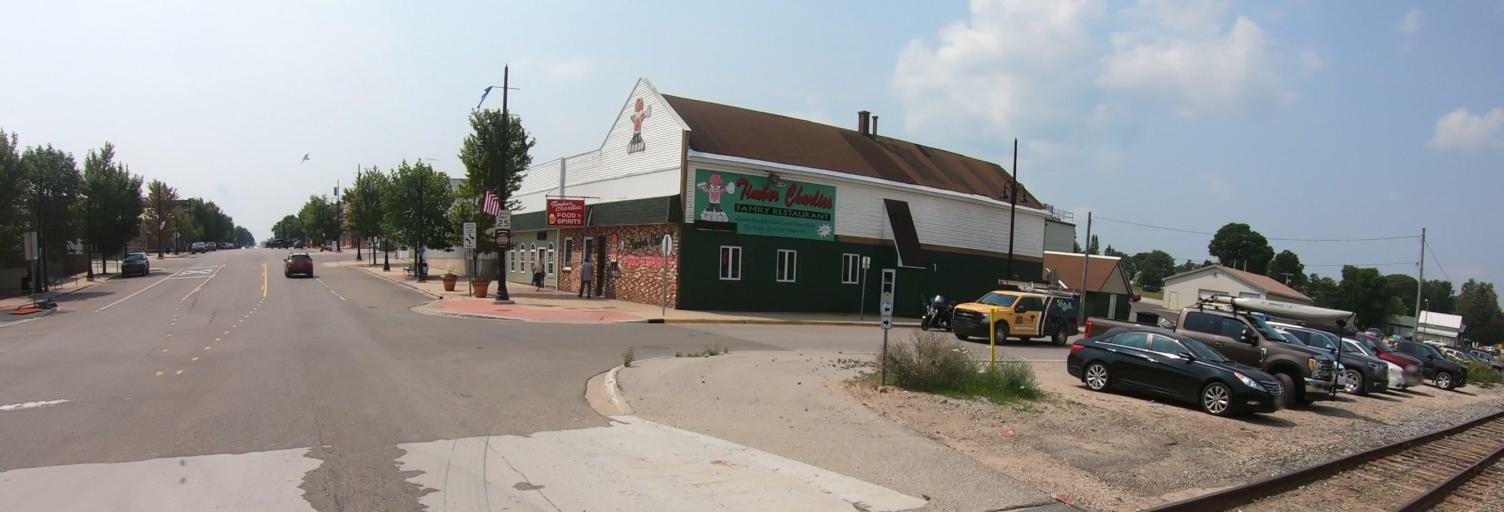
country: US
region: Michigan
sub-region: Luce County
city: Newberry
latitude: 46.3567
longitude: -85.5098
